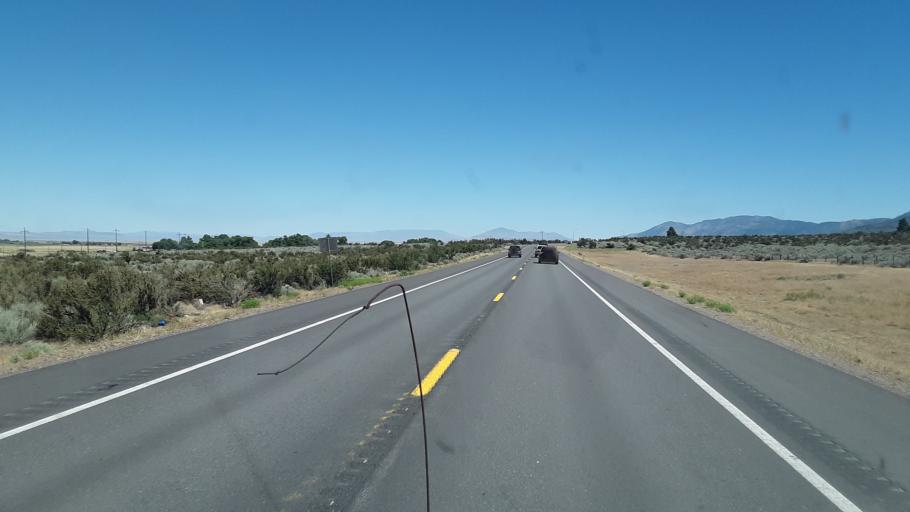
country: US
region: California
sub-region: Lassen County
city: Janesville
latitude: 40.2875
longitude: -120.4964
